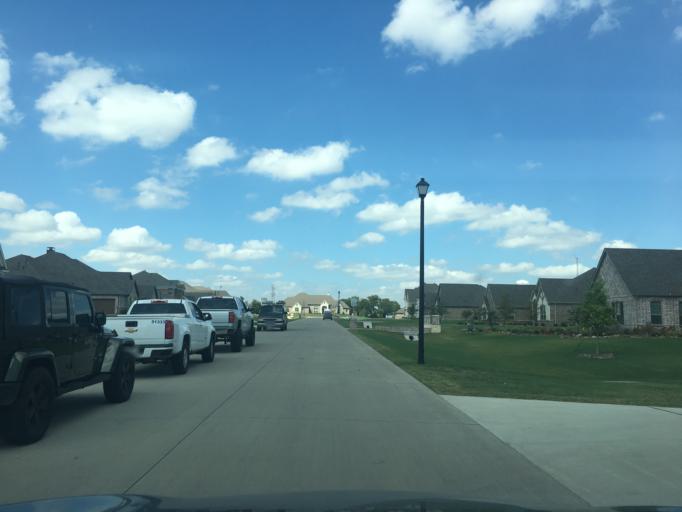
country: US
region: Texas
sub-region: Dallas County
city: Sachse
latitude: 32.9658
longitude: -96.5570
